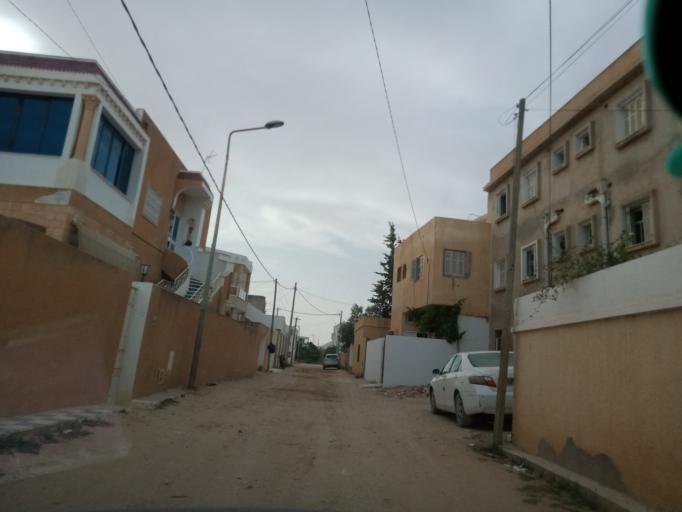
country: TN
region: Safaqis
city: Al Qarmadah
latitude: 34.8039
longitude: 10.7521
